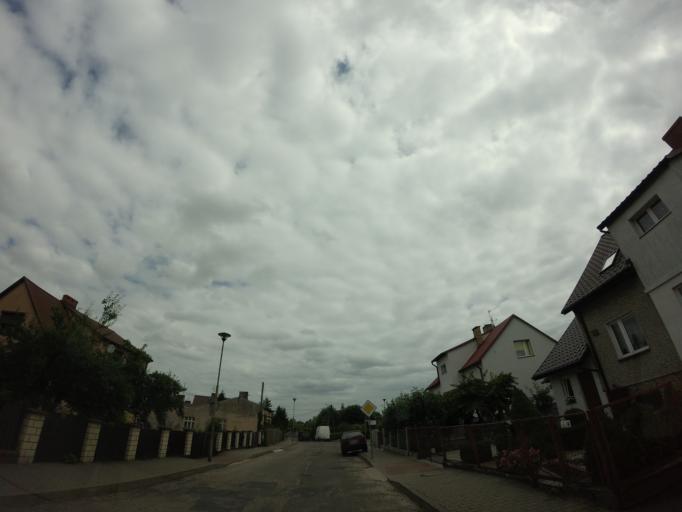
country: PL
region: Lubusz
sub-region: Powiat strzelecko-drezdenecki
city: Strzelce Krajenskie
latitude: 52.8771
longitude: 15.5372
